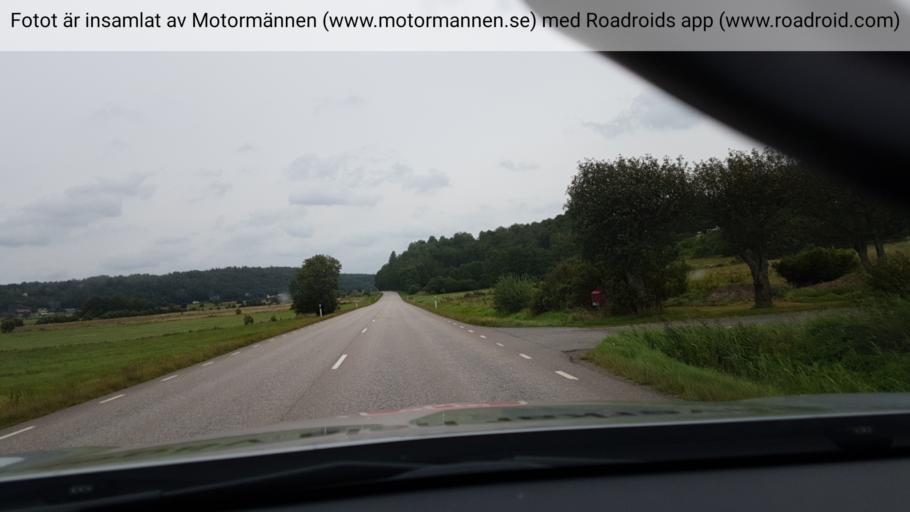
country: SE
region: Vaestra Goetaland
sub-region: Molndal
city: Lindome
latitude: 57.5952
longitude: 12.1455
